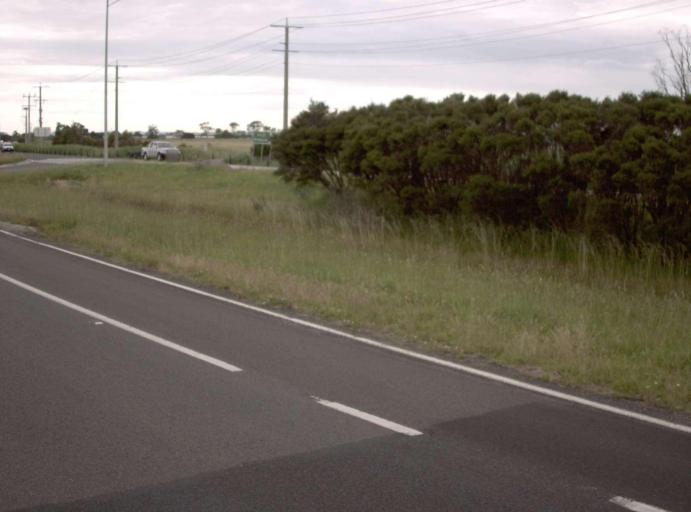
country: AU
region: Victoria
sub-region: Cardinia
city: Koo-Wee-Rup
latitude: -38.2118
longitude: 145.4677
